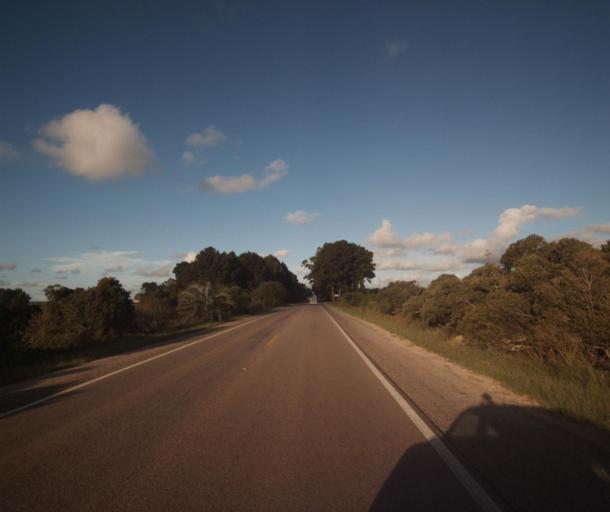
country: BR
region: Rio Grande do Sul
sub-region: Rio Grande
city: Rio Grande
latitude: -32.0952
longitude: -52.3144
